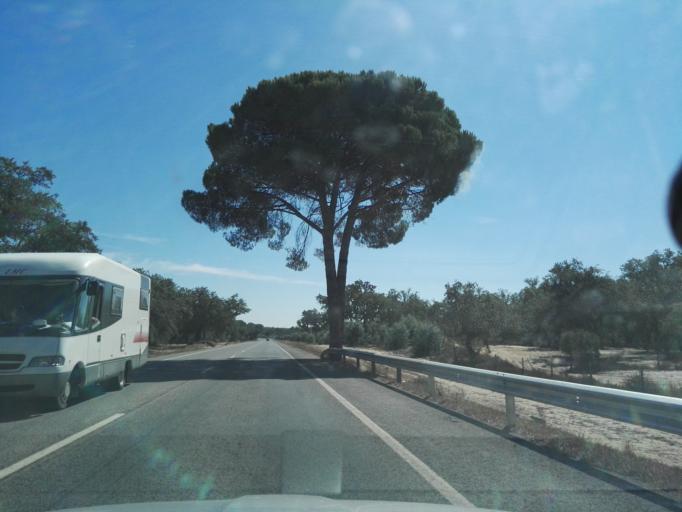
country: PT
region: Santarem
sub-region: Benavente
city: Poceirao
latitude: 38.8754
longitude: -8.8070
